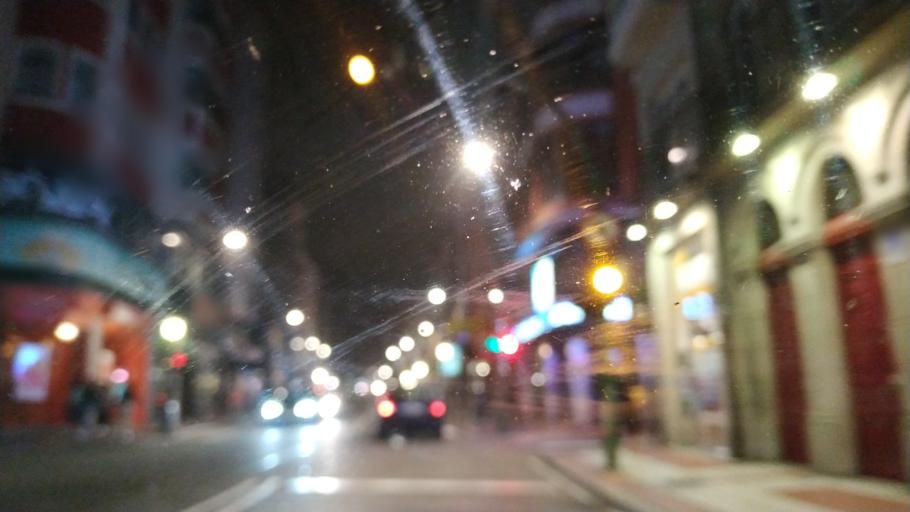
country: ES
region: Galicia
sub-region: Provincia da Coruna
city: A Coruna
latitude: 43.3698
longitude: -8.4031
